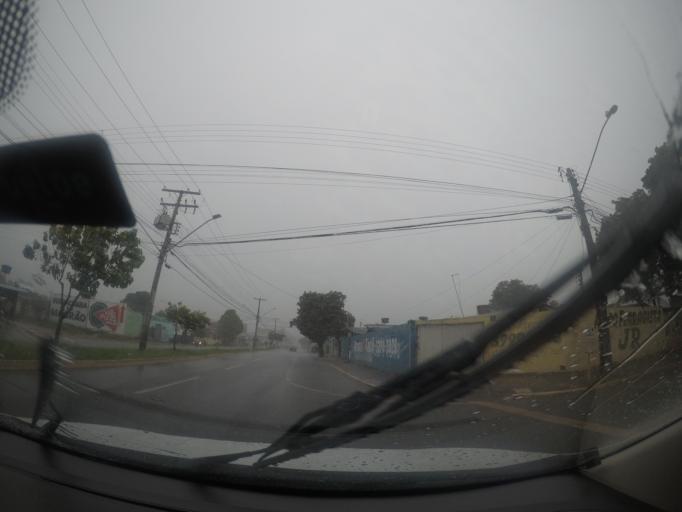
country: BR
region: Goias
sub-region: Goiania
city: Goiania
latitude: -16.6190
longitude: -49.3564
